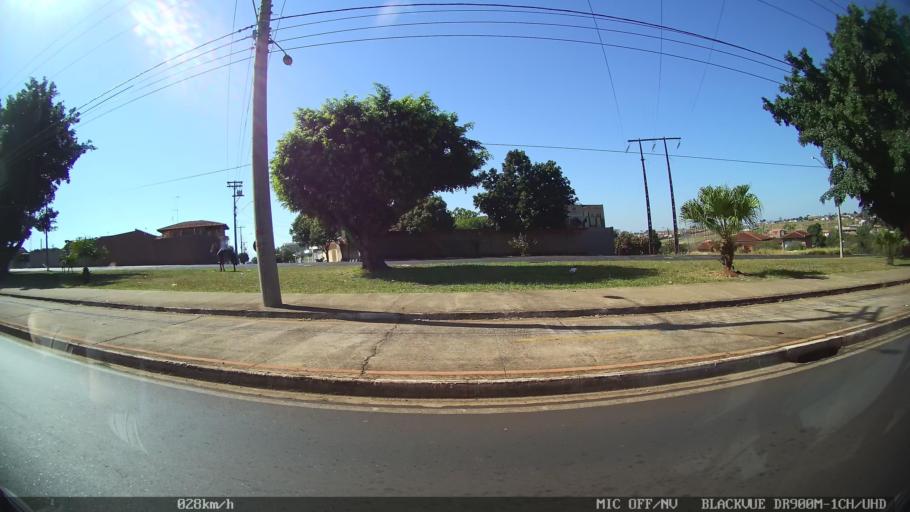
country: BR
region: Sao Paulo
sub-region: Batatais
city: Batatais
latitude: -20.9060
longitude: -47.5822
